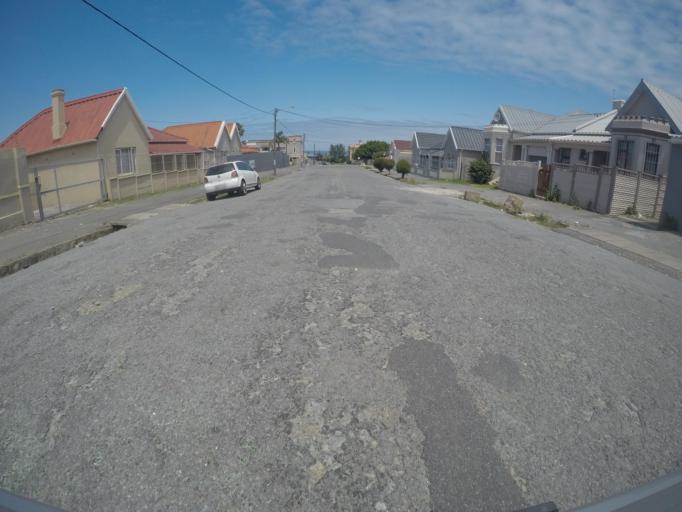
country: ZA
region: Eastern Cape
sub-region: Buffalo City Metropolitan Municipality
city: East London
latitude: -33.0193
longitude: 27.9128
